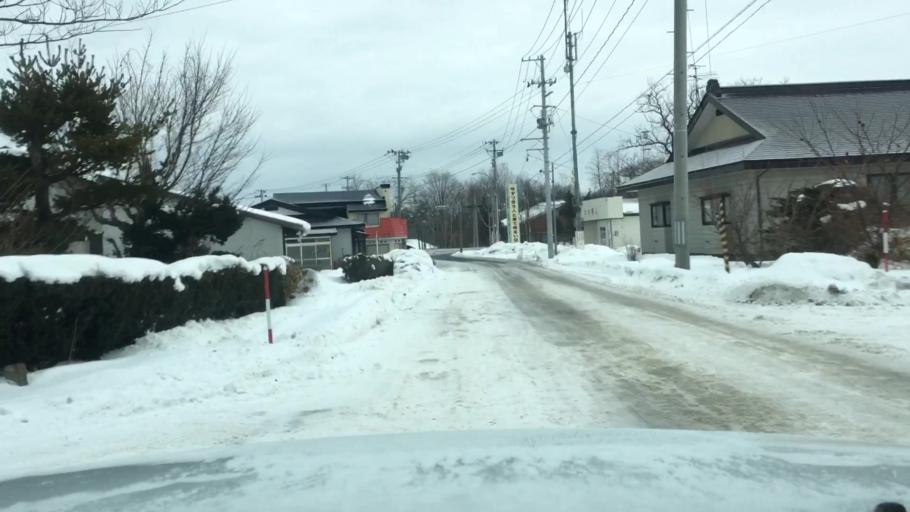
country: JP
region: Iwate
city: Shizukuishi
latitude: 39.9156
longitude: 141.0056
